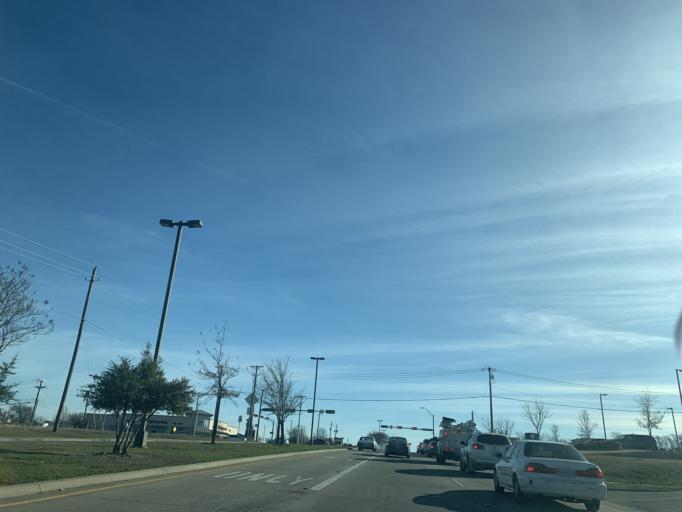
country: US
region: Texas
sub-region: Dallas County
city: Shamrock
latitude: 32.5897
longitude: -96.8754
